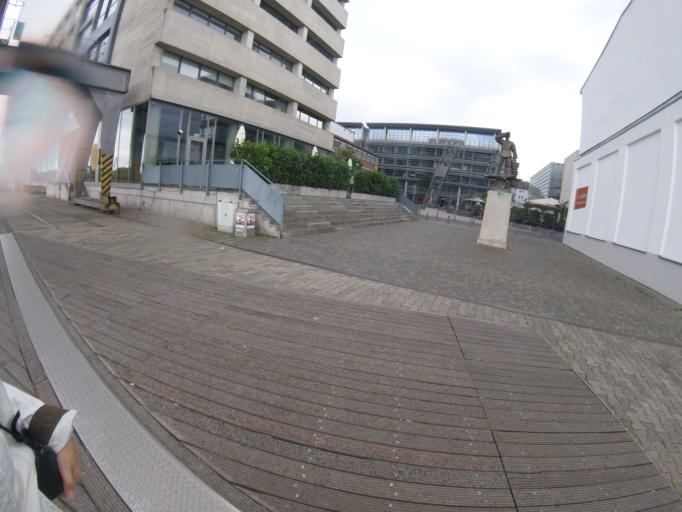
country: DE
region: North Rhine-Westphalia
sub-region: Regierungsbezirk Dusseldorf
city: Dusseldorf
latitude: 51.2154
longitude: 6.7542
